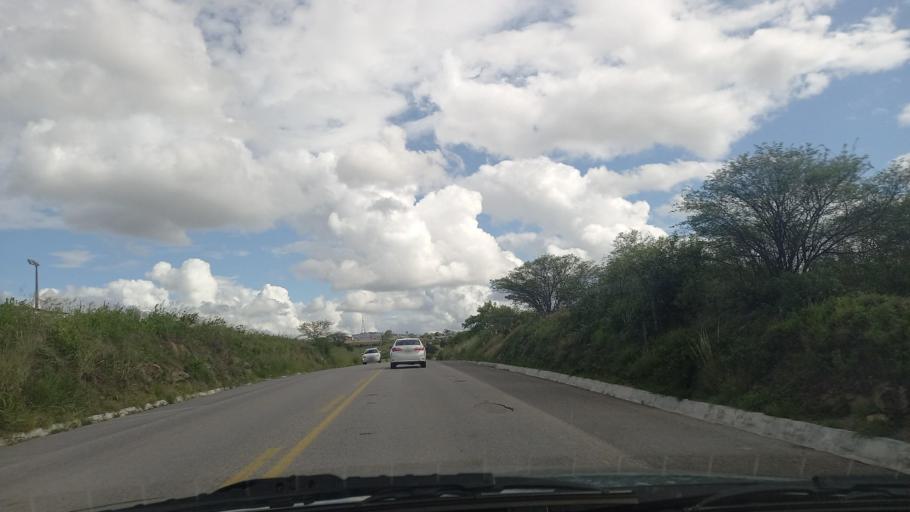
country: BR
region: Pernambuco
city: Garanhuns
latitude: -8.8233
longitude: -36.4498
